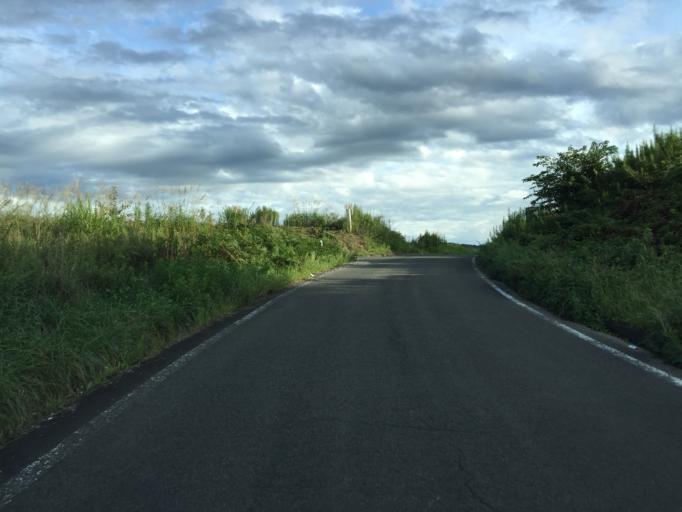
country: JP
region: Fukushima
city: Hobaramachi
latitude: 37.8038
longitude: 140.5410
